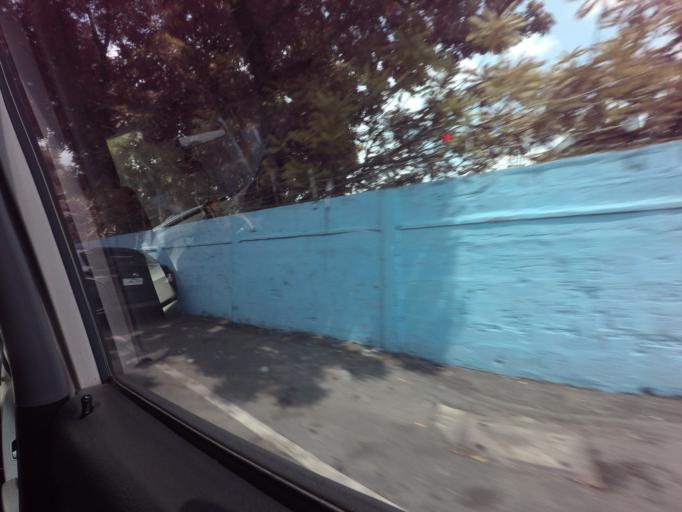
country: PH
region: Metro Manila
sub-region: San Juan
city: San Juan
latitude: 14.5897
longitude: 121.0123
